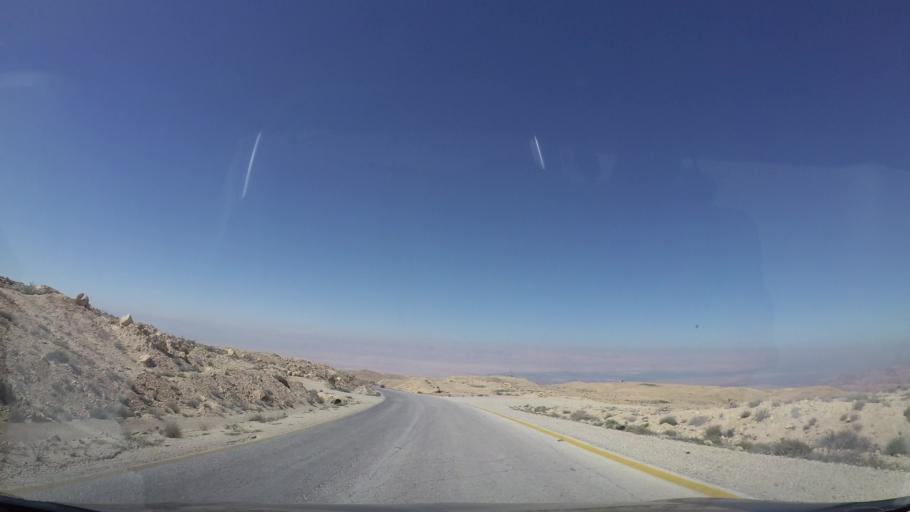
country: JO
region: Tafielah
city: At Tafilah
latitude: 30.8602
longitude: 35.5387
